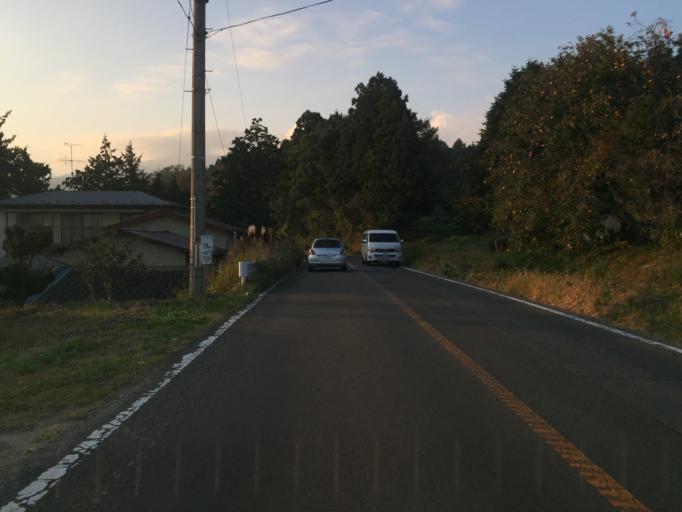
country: JP
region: Fukushima
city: Motomiya
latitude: 37.5505
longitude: 140.3642
